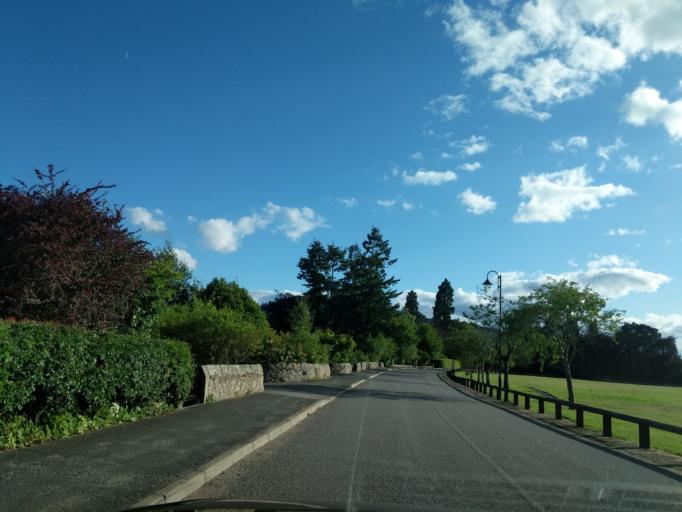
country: GB
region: Scotland
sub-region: Aberdeenshire
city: Aboyne
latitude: 57.0736
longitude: -2.7808
